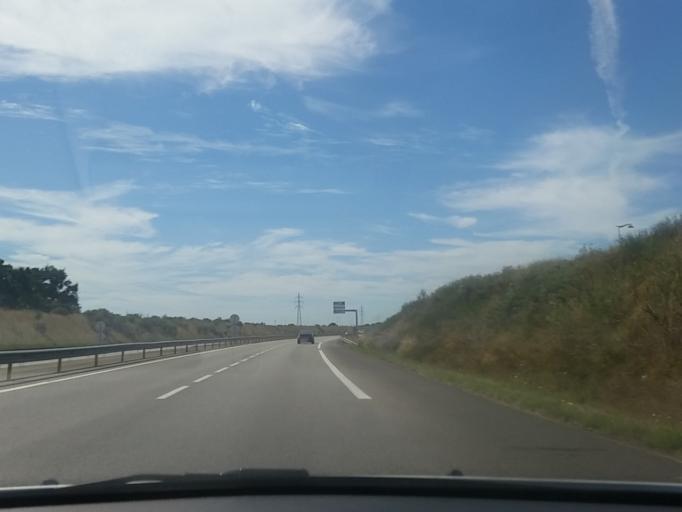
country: FR
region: Pays de la Loire
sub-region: Departement de la Loire-Atlantique
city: La Montagne
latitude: 47.1754
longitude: -1.6953
